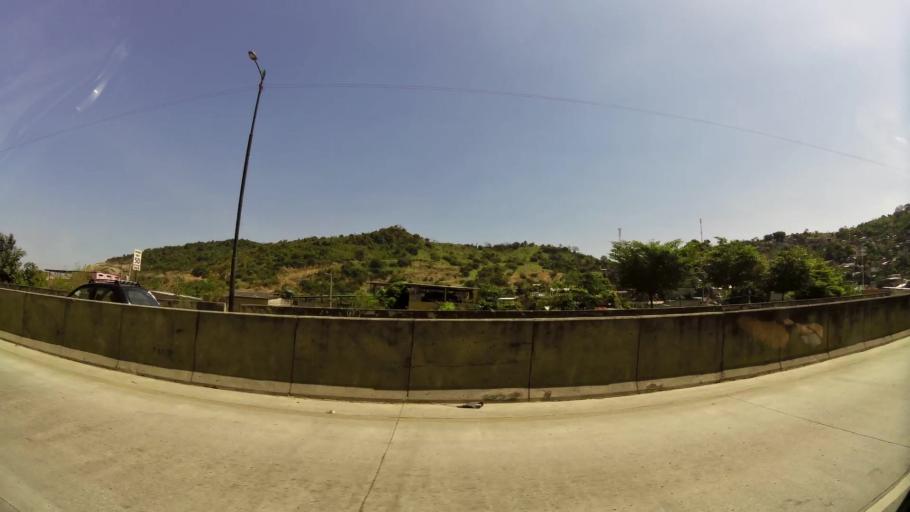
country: EC
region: Guayas
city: Guayaquil
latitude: -2.1793
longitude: -79.9270
